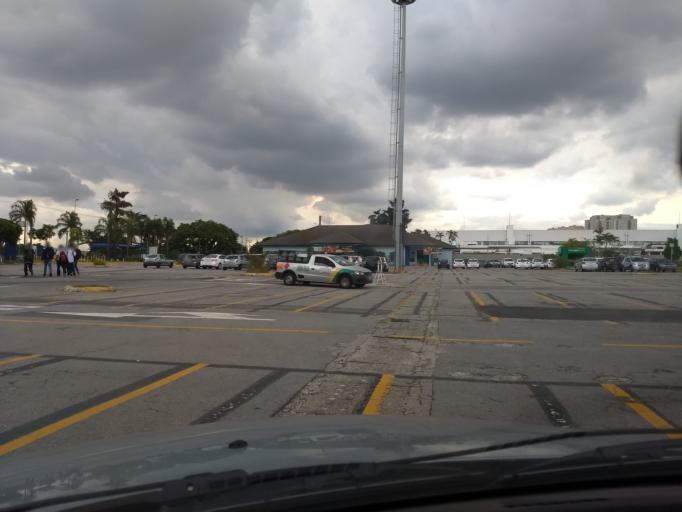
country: BR
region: Sao Paulo
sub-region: Sao Paulo
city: Sao Paulo
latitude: -23.5234
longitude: -46.5996
